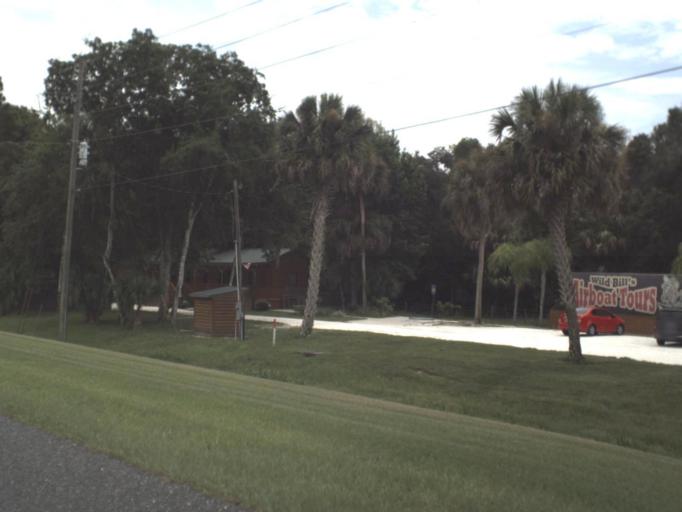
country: US
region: Florida
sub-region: Citrus County
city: Inverness
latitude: 28.8511
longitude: -82.2254
